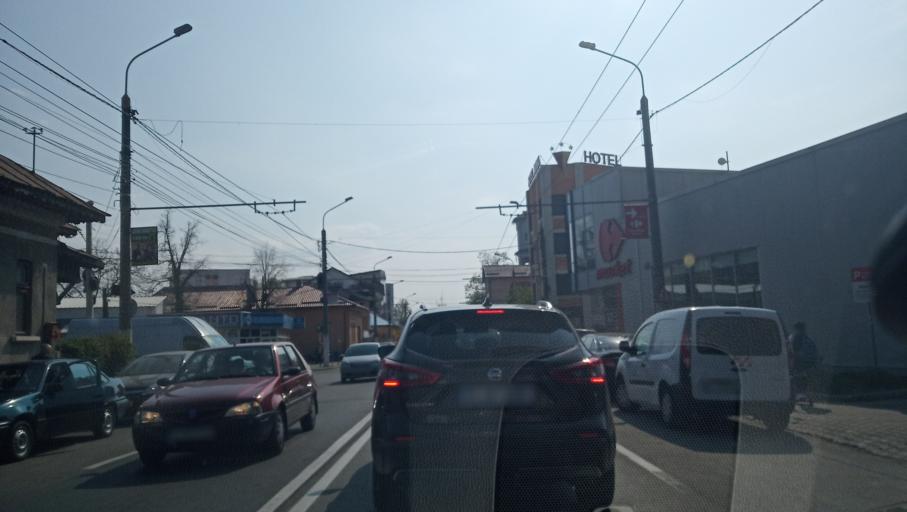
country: RO
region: Gorj
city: Targu Jiu
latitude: 45.0457
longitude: 23.2766
